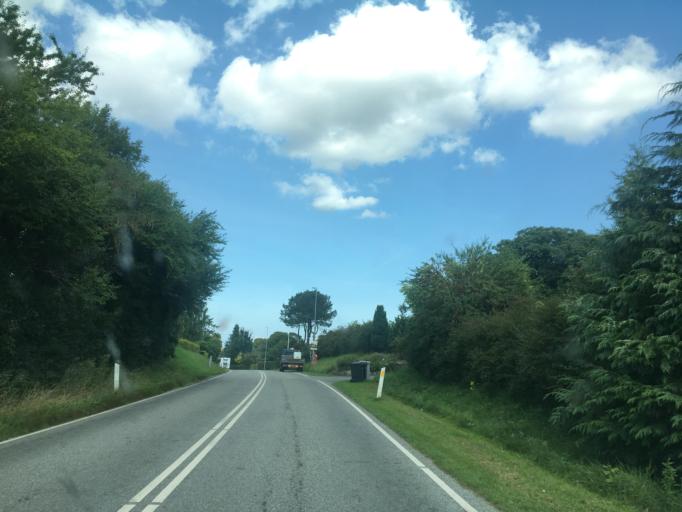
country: DK
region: South Denmark
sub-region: Middelfart Kommune
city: Ejby
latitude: 55.4199
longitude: 9.9217
